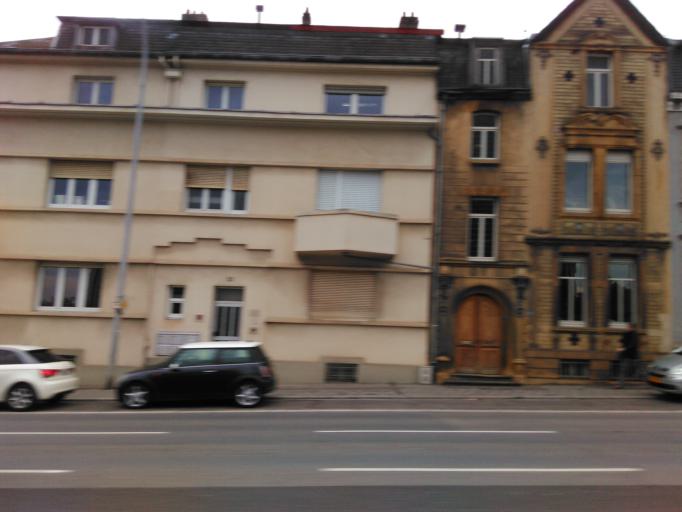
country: LU
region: Luxembourg
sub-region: Canton de Luxembourg
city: Luxembourg
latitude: 49.6019
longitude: 6.1203
